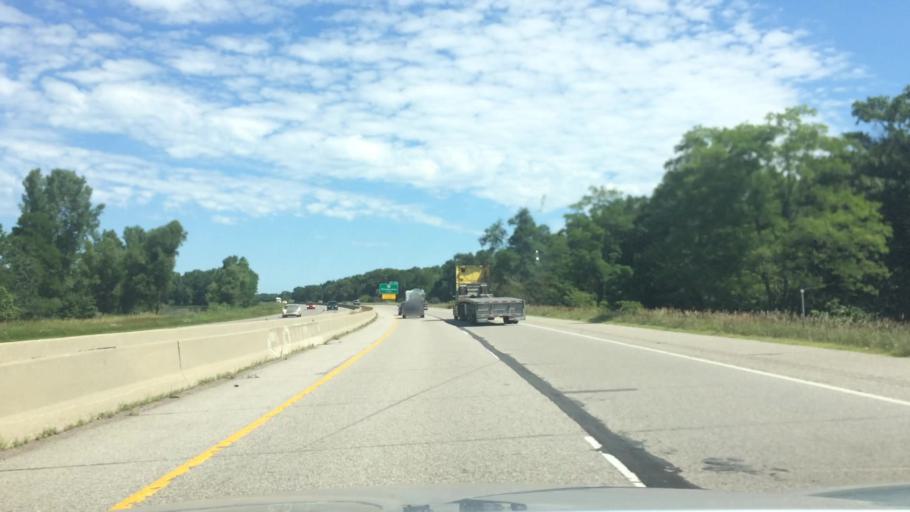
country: US
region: Wisconsin
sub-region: Marquette County
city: Westfield
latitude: 43.7383
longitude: -89.4831
